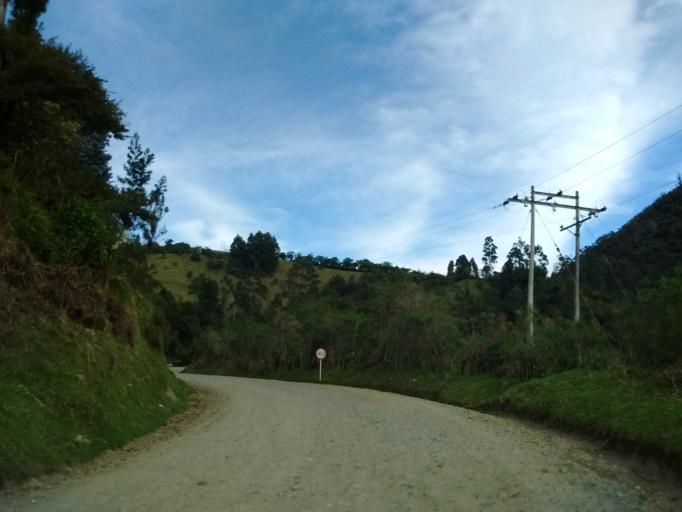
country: CO
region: Cauca
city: Totoro
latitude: 2.3819
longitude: -76.4511
